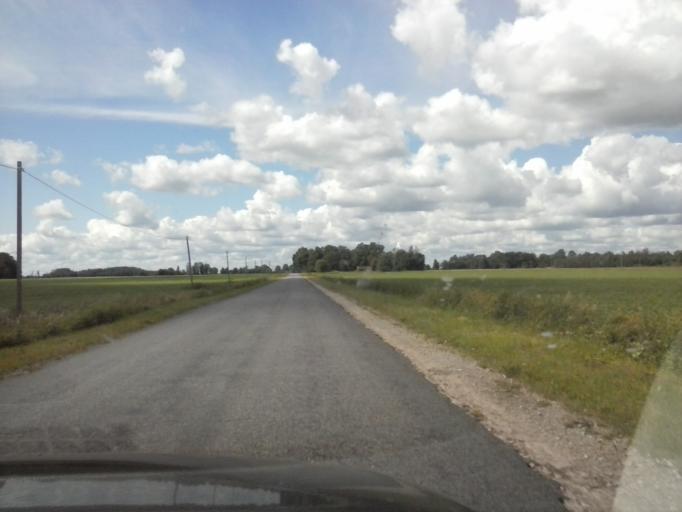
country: EE
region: Laeaene-Virumaa
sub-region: Rakke vald
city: Rakke
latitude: 59.0522
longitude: 26.3628
